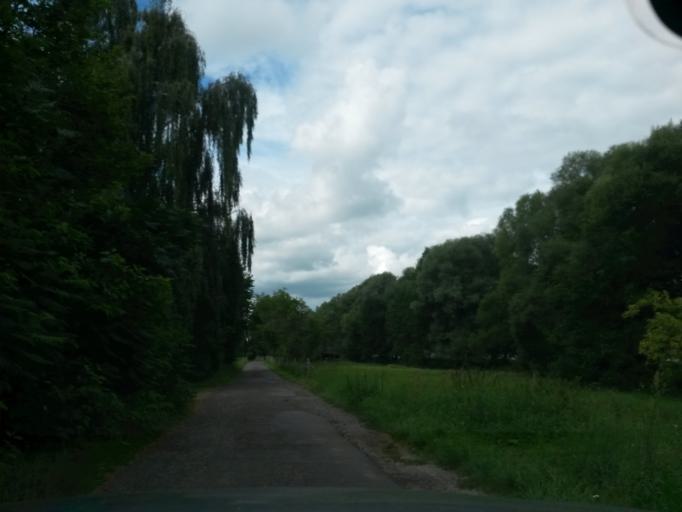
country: DE
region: Brandenburg
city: Oderberg
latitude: 52.8693
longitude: 14.1032
